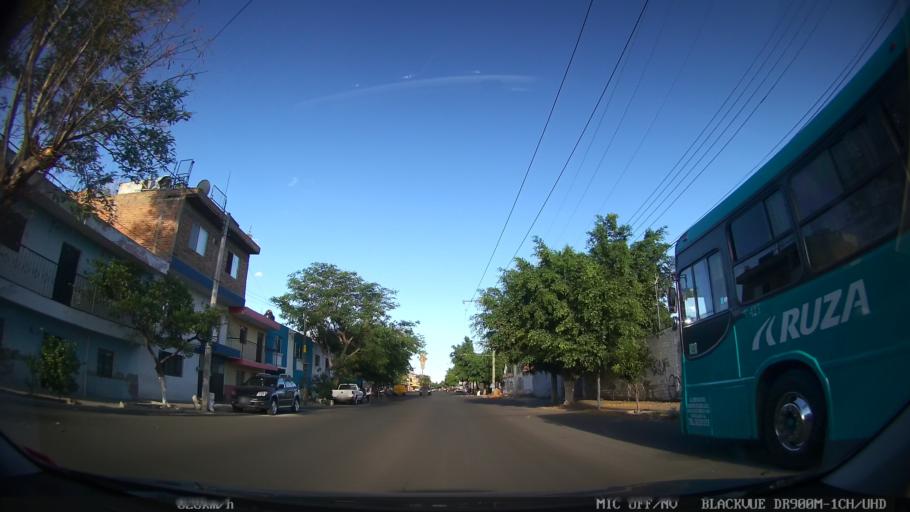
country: MX
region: Jalisco
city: Tlaquepaque
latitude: 20.7081
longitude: -103.3005
